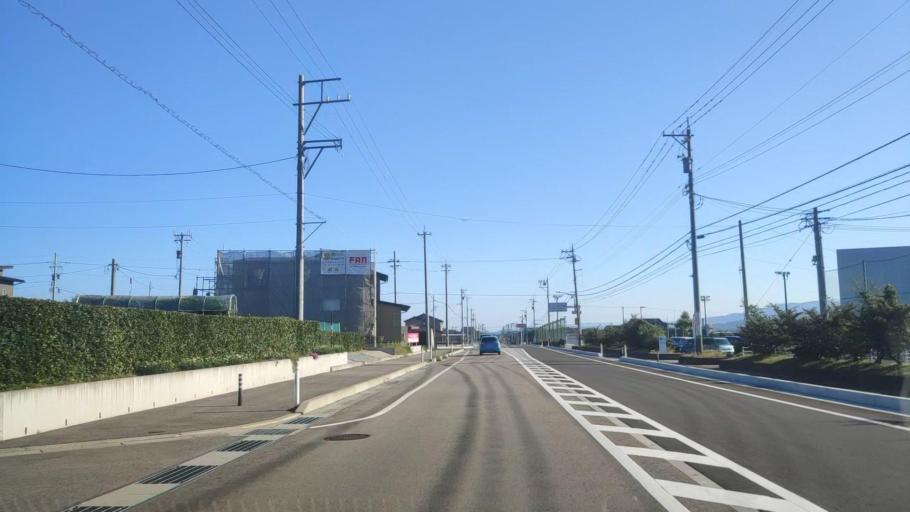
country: JP
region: Ishikawa
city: Tsubata
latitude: 36.7343
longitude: 136.7013
